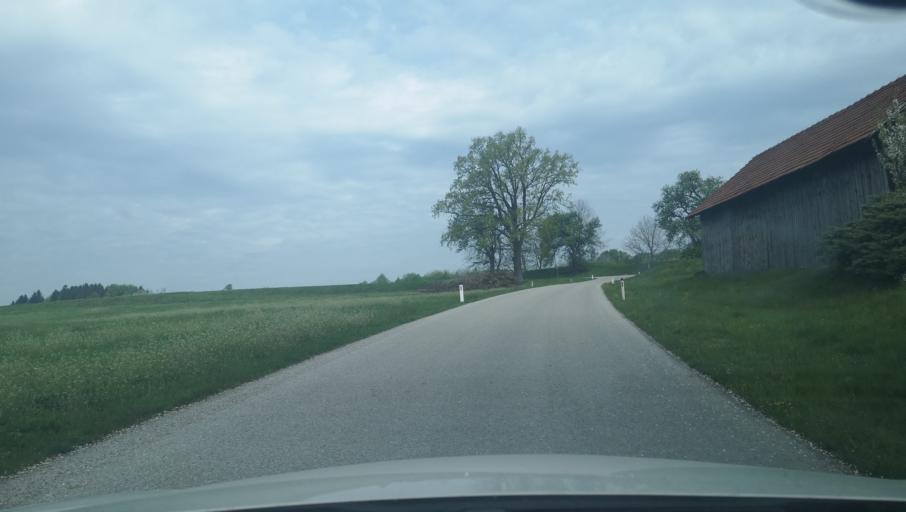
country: AT
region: Lower Austria
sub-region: Politischer Bezirk Melk
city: Blindenmarkt
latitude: 48.1349
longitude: 14.9695
